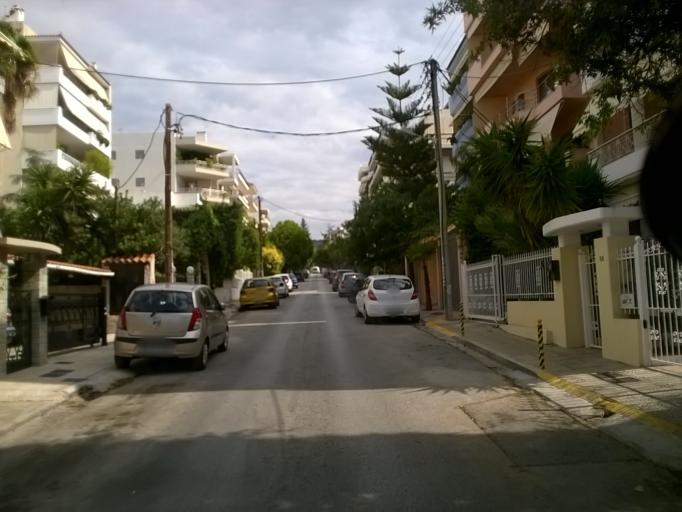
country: GR
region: Attica
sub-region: Nomarchia Athinas
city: Glyfada
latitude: 37.8843
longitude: 23.7633
